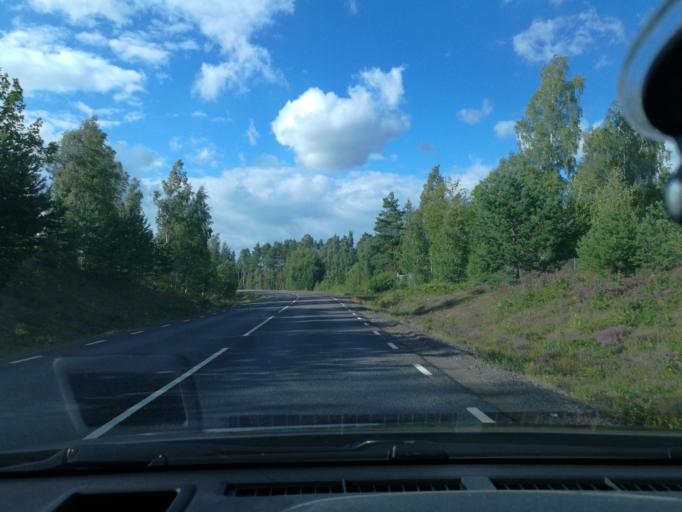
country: SE
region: Kronoberg
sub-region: Vaxjo Kommun
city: Braas
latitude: 57.0571
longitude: 15.0383
